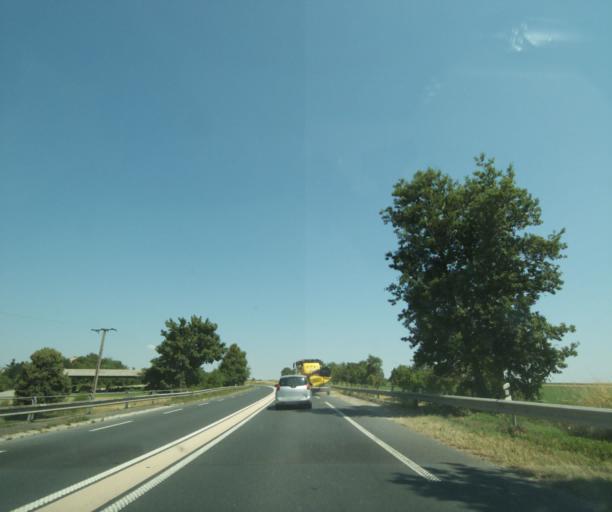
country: FR
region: Champagne-Ardenne
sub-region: Departement de la Marne
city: Mourmelon-le-Grand
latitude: 49.0647
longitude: 4.2971
